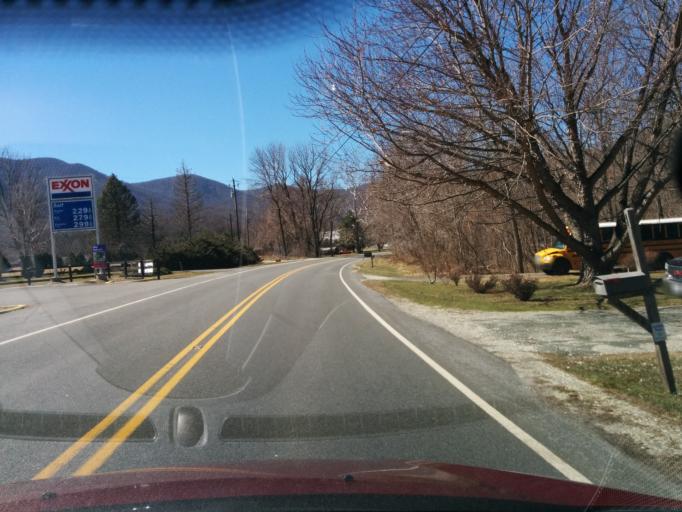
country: US
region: Virginia
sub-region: Nelson County
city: Nellysford
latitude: 37.8750
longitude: -78.9361
